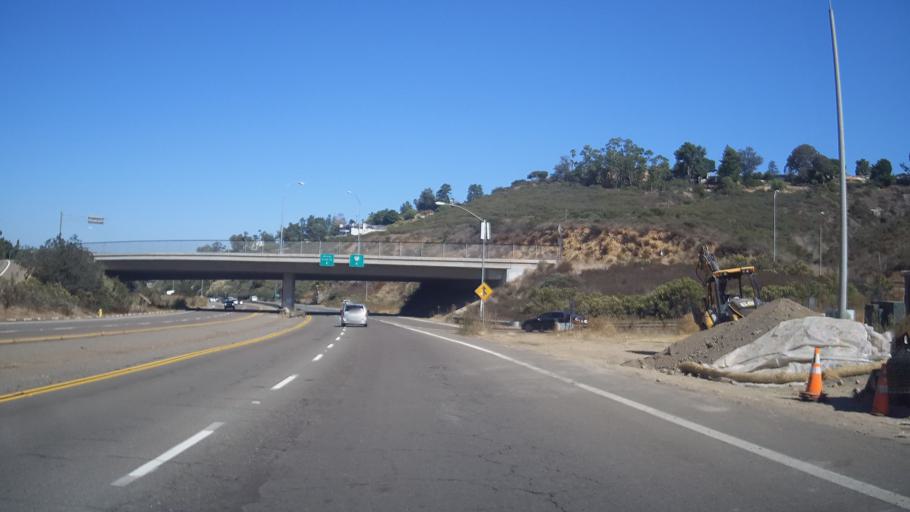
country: US
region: California
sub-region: San Diego County
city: Lemon Grove
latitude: 32.7715
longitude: -117.0969
